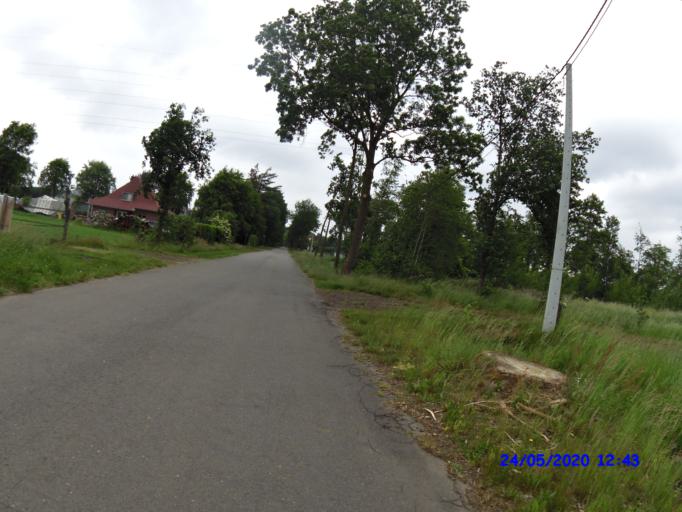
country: BE
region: Flanders
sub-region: Provincie Antwerpen
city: Retie
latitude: 51.2202
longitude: 5.0402
